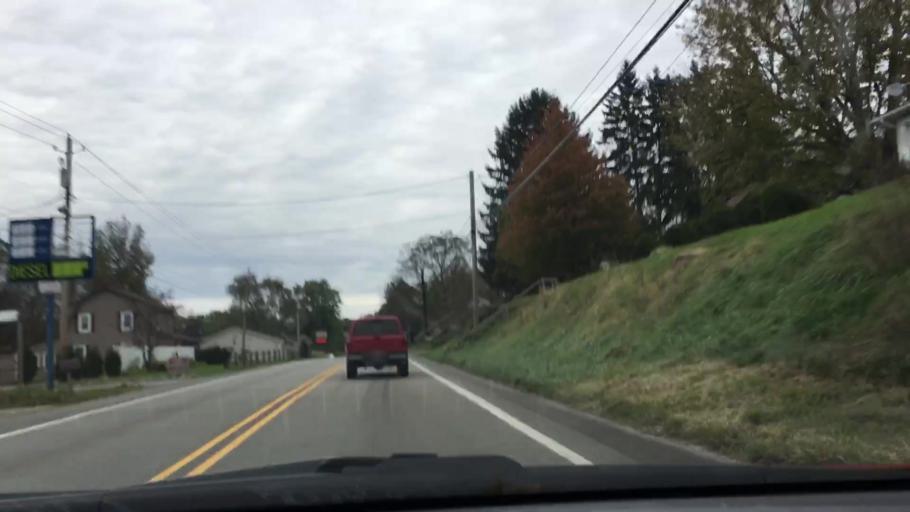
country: US
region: Pennsylvania
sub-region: Armstrong County
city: Orchard Hills
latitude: 40.5869
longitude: -79.5292
